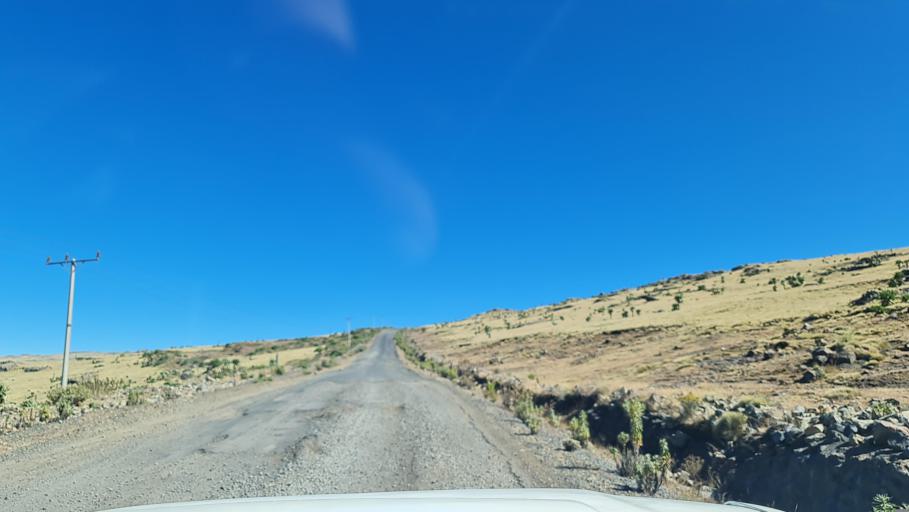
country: ET
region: Amhara
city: Debark'
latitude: 13.1639
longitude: 38.1946
